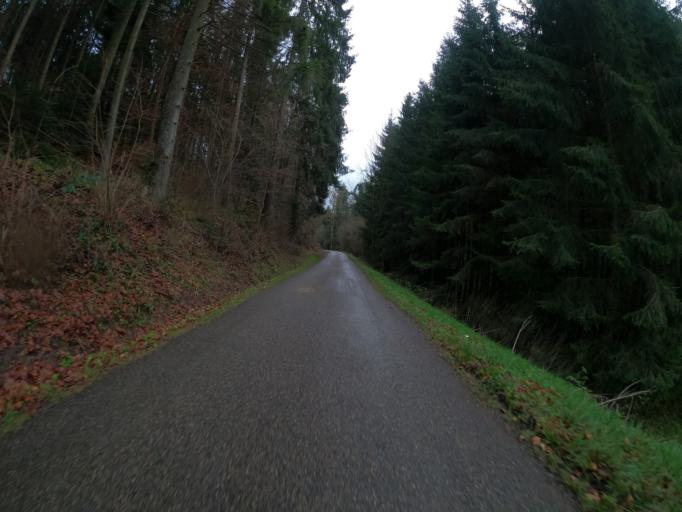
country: DE
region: Baden-Wuerttemberg
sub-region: Regierungsbezirk Stuttgart
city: Lorch
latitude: 48.7854
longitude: 9.7229
